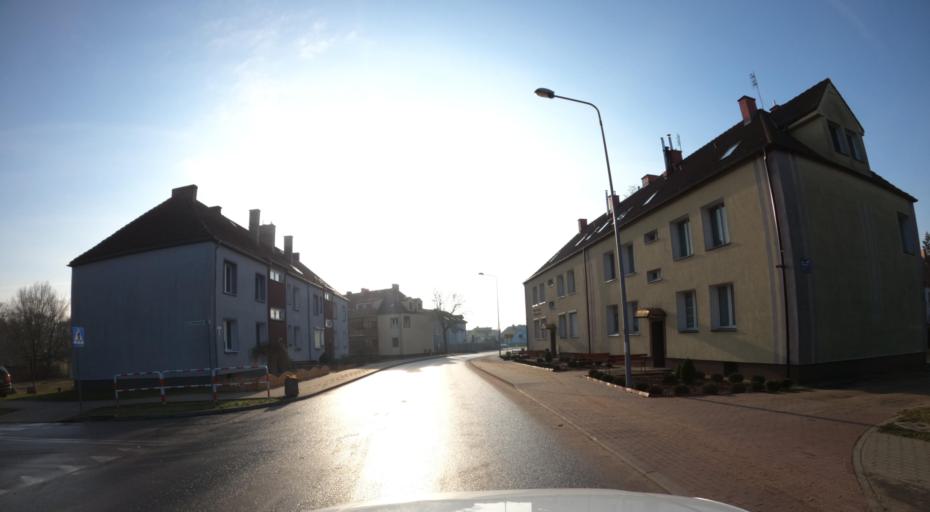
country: PL
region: Lubusz
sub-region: Powiat gorzowski
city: Kostrzyn nad Odra
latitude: 52.6059
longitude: 14.6358
